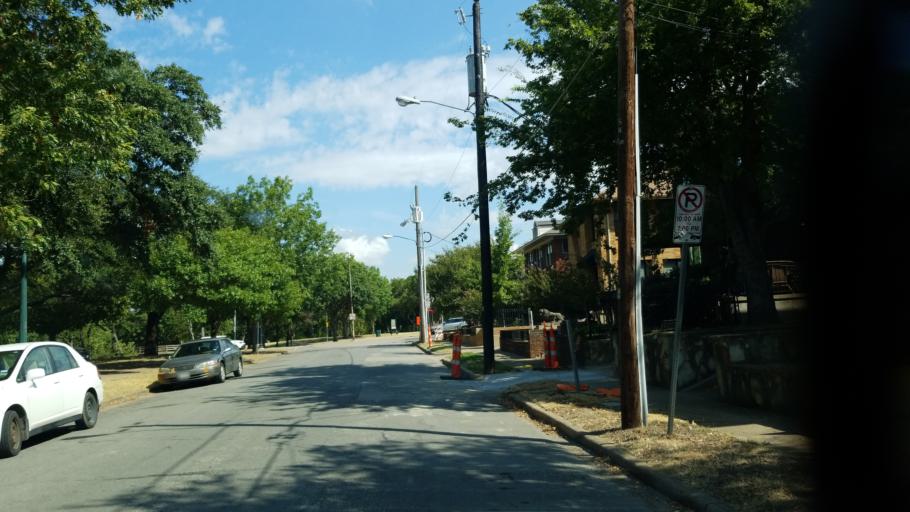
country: US
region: Texas
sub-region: Dallas County
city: Dallas
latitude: 32.7582
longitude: -96.8168
